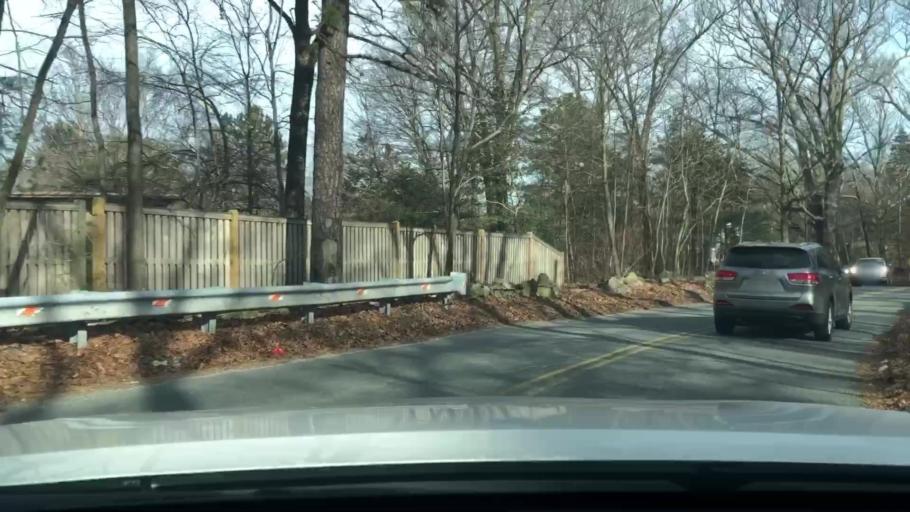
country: US
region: Massachusetts
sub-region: Worcester County
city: Milford
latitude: 42.1361
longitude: -71.4903
